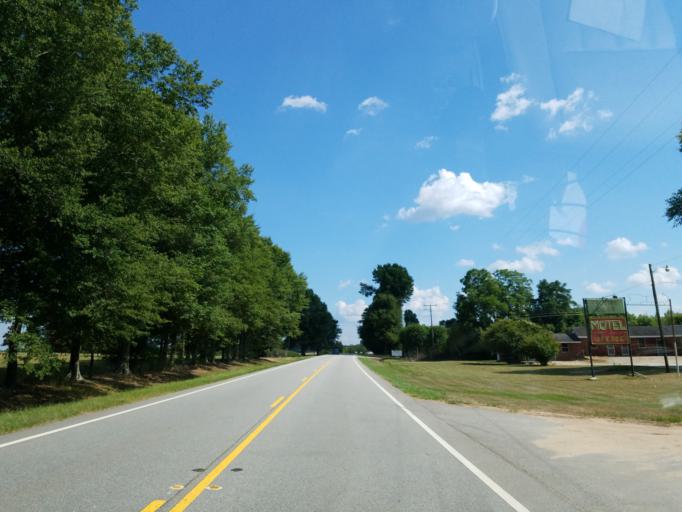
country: US
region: Georgia
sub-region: Lamar County
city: Barnesville
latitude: 32.9697
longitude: -84.1126
